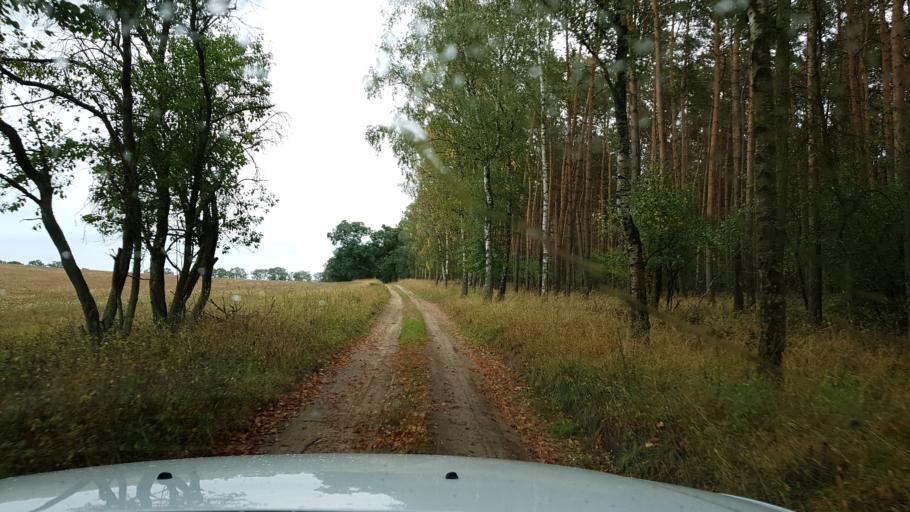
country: PL
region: West Pomeranian Voivodeship
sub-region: Powiat gryfinski
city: Cedynia
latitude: 52.8369
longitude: 14.2902
